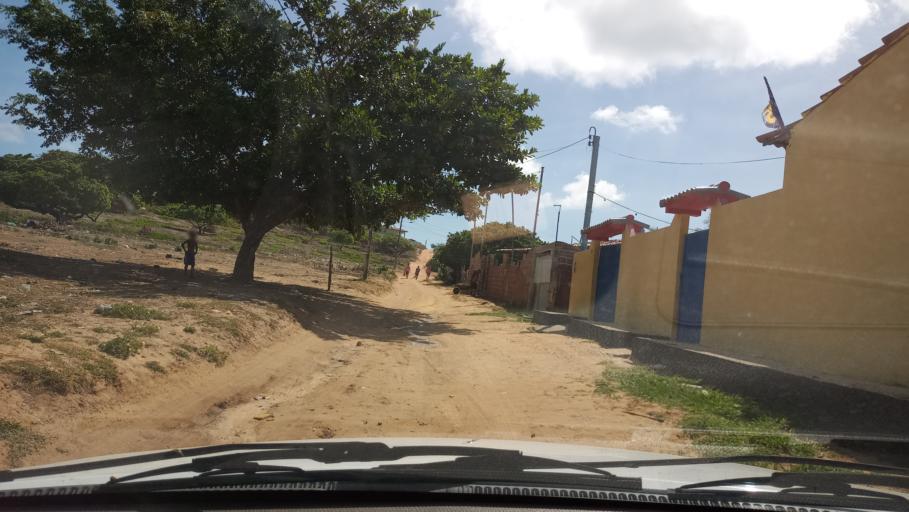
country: BR
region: Rio Grande do Norte
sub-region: Maxaranguape
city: Sao Miguel
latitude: -5.5132
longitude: -35.2649
